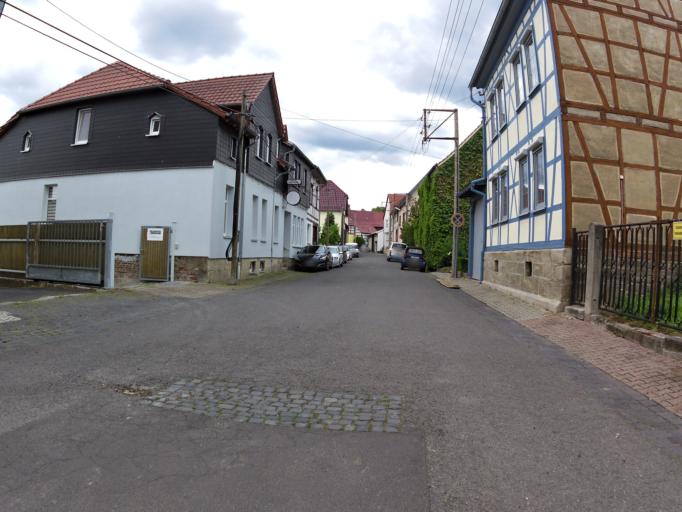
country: DE
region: Thuringia
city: Oberdorla
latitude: 51.1663
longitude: 10.4227
